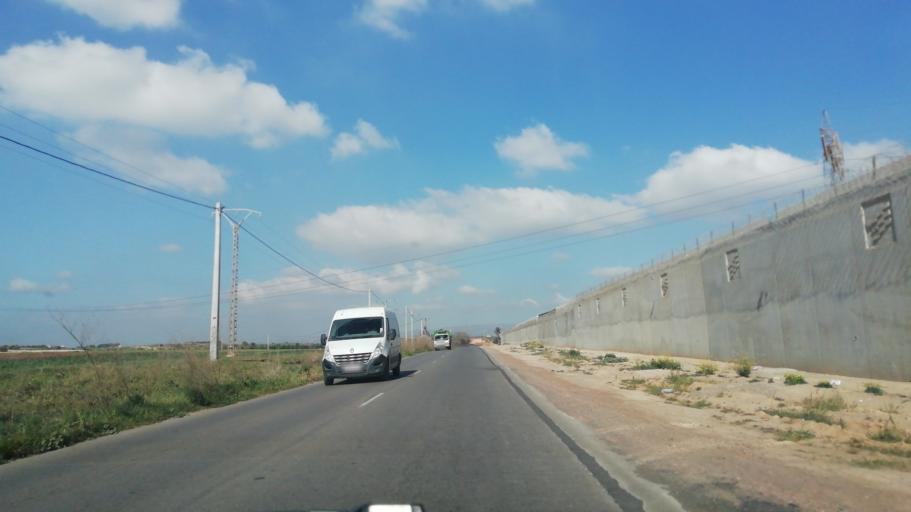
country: DZ
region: Oran
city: Ain el Bya
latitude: 35.7536
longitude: -0.2692
